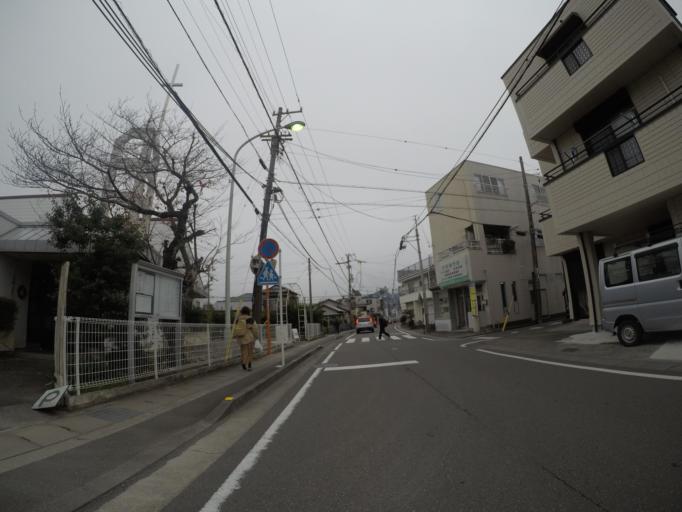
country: JP
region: Shizuoka
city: Shizuoka-shi
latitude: 34.9933
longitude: 138.4186
